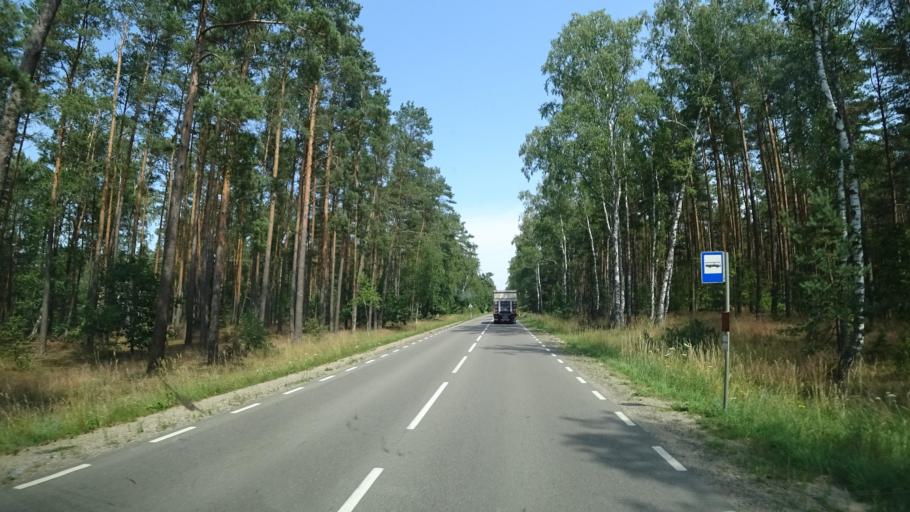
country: PL
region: Pomeranian Voivodeship
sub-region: Powiat koscierski
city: Lipusz
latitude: 54.0989
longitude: 17.8155
